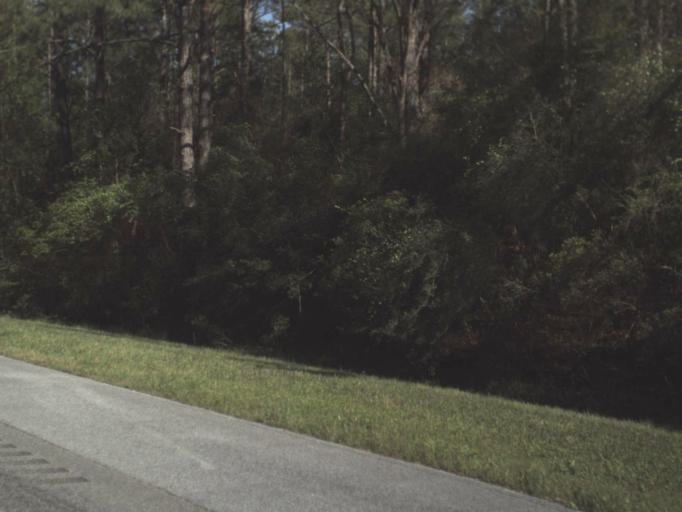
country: US
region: Florida
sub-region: Okaloosa County
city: Crestview
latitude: 30.7182
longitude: -86.4321
